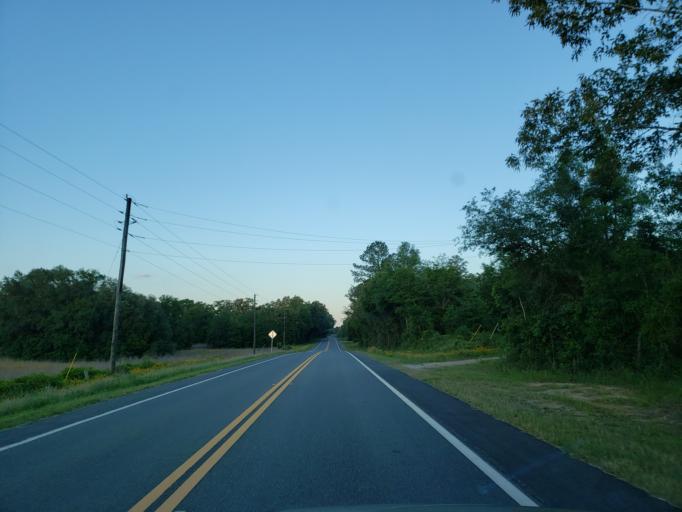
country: US
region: Florida
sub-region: Madison County
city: Madison
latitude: 30.5813
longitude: -83.2232
